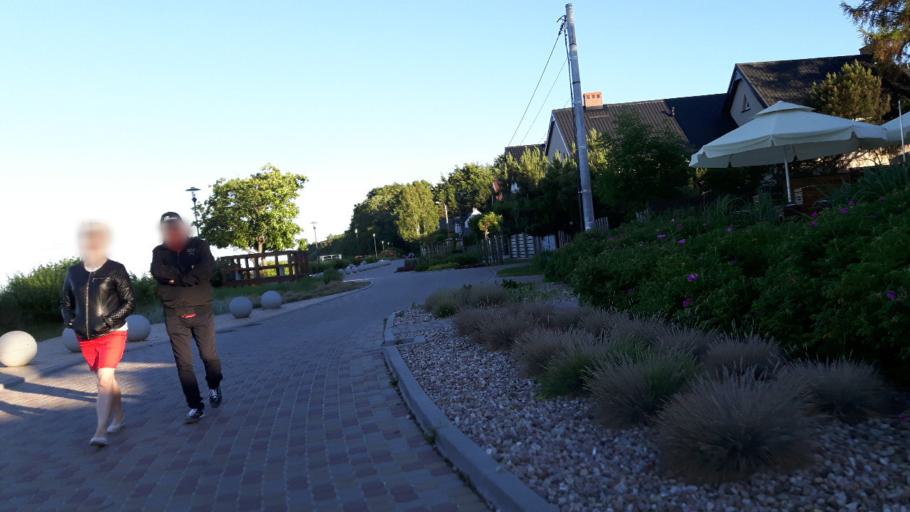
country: PL
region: Pomeranian Voivodeship
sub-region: Powiat pucki
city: Mosty
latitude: 54.6086
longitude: 18.5143
